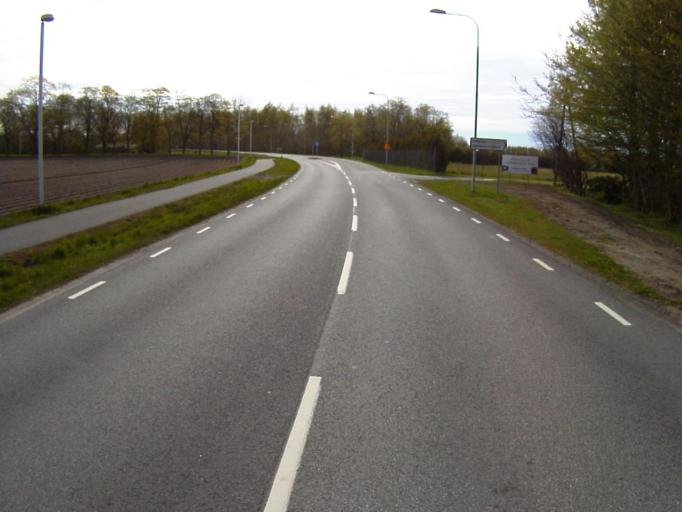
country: SE
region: Skane
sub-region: Kristianstads Kommun
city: Norra Asum
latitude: 56.0029
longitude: 14.1382
